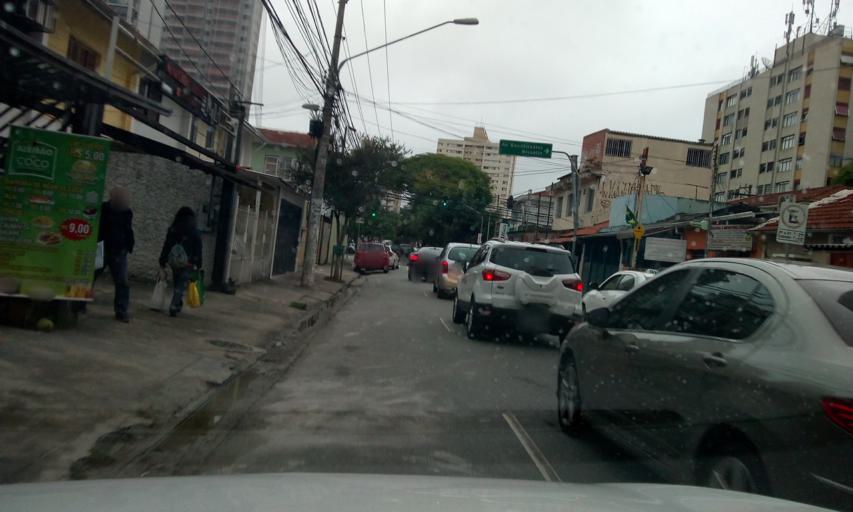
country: BR
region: Sao Paulo
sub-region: Sao Paulo
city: Sao Paulo
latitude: -23.5987
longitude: -46.6803
